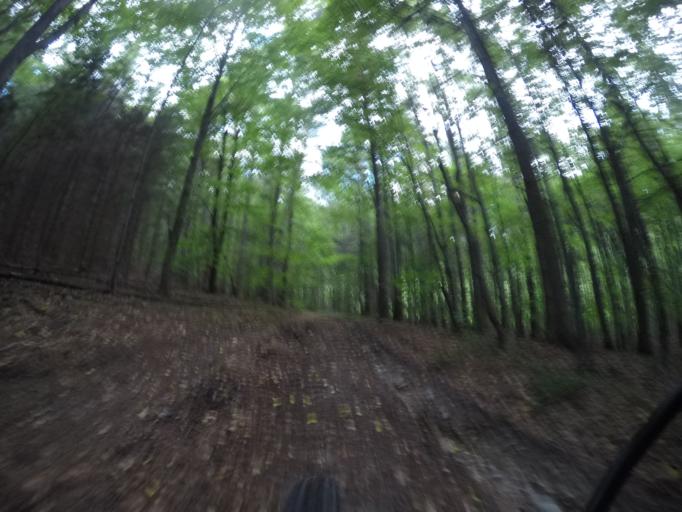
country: SK
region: Kosicky
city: Gelnica
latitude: 48.9250
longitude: 21.0292
